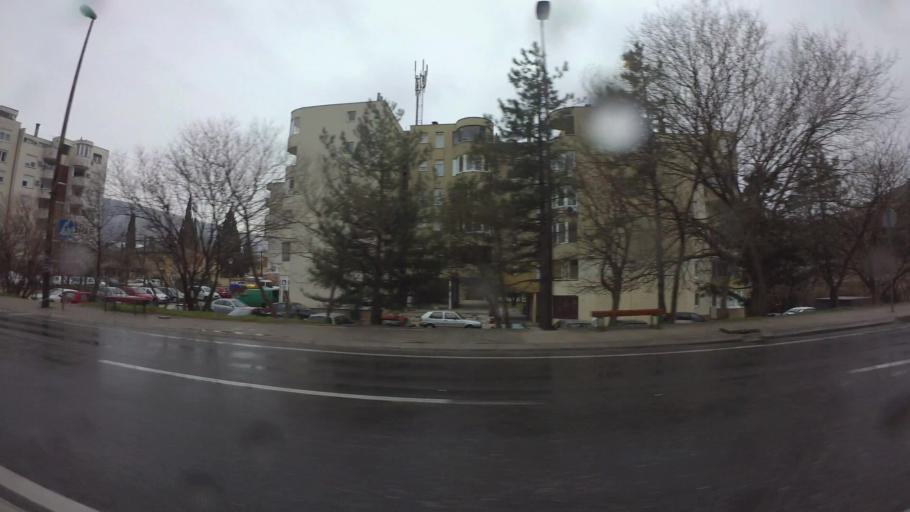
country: BA
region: Federation of Bosnia and Herzegovina
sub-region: Hercegovacko-Bosanski Kanton
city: Mostar
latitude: 43.3268
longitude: 17.8197
